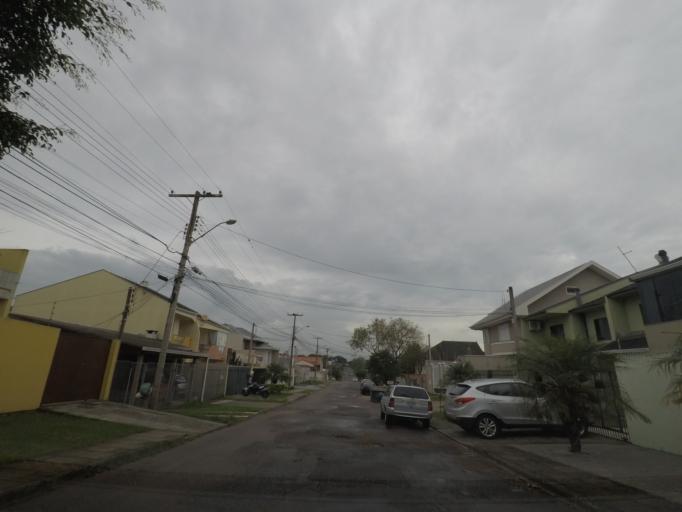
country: BR
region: Parana
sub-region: Curitiba
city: Curitiba
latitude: -25.4730
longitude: -49.3136
